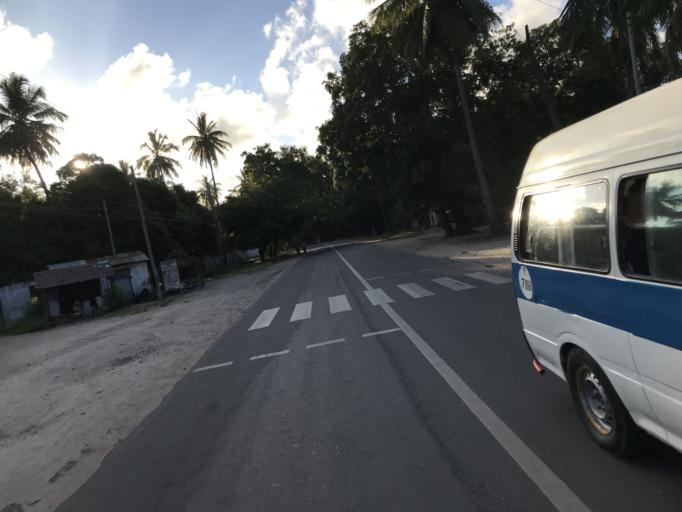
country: TZ
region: Dar es Salaam
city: Dar es Salaam
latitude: -6.8651
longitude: 39.3637
